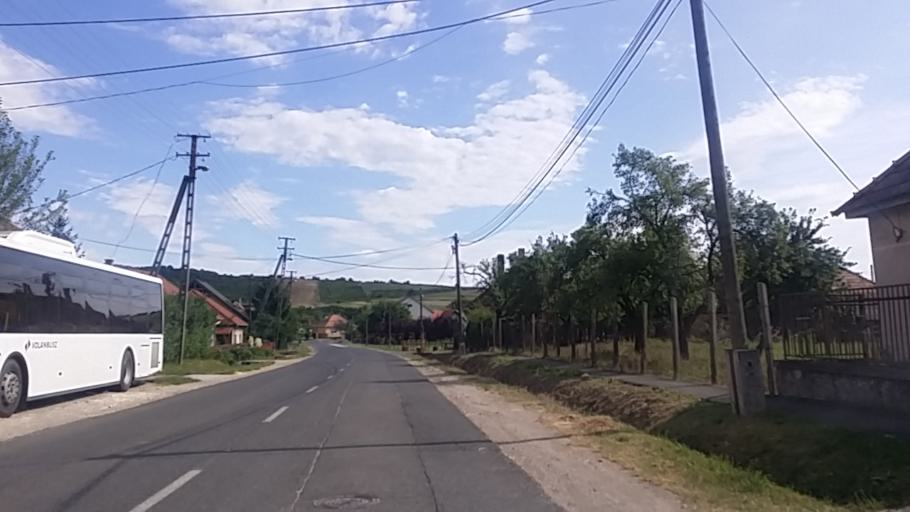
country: HU
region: Pest
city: Kosd
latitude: 47.8351
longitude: 19.2341
